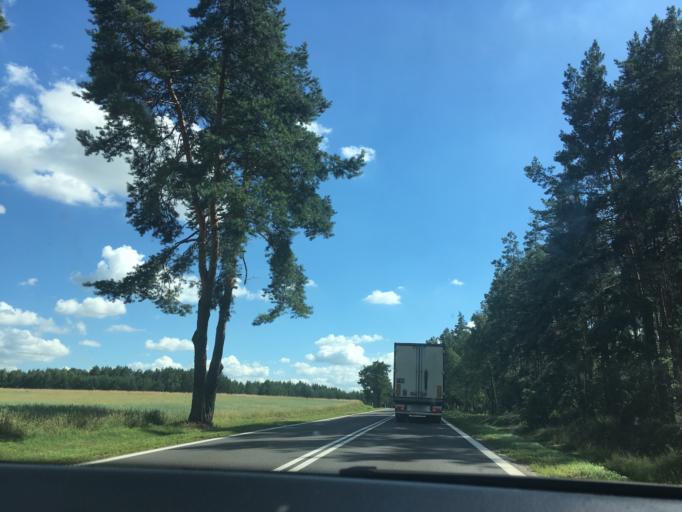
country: PL
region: Podlasie
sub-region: Powiat sokolski
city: Suchowola
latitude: 53.6465
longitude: 23.1196
